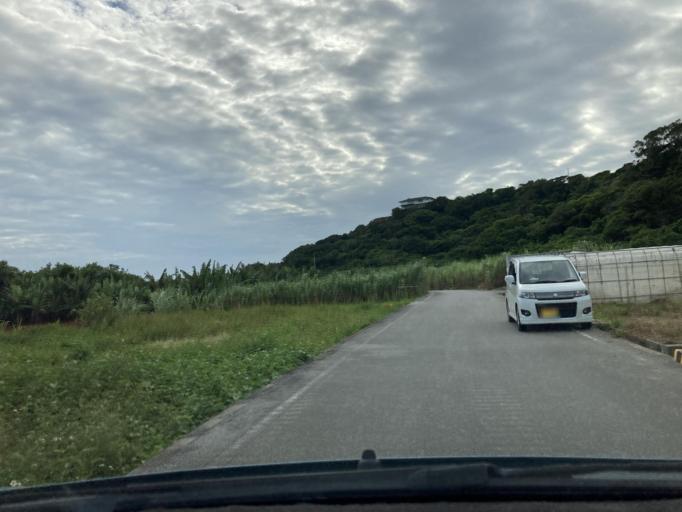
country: JP
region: Okinawa
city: Tomigusuku
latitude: 26.1388
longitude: 127.7949
